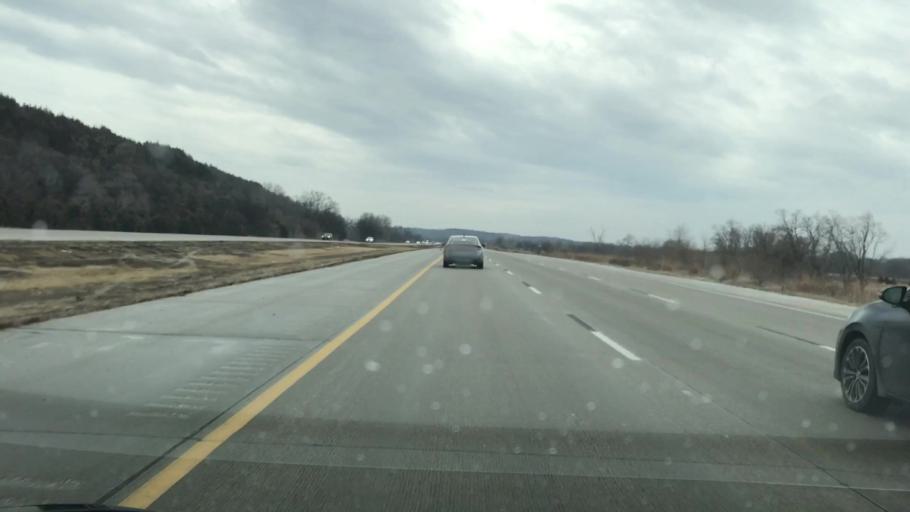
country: US
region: Nebraska
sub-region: Saunders County
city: Ashland
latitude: 41.0489
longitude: -96.2964
